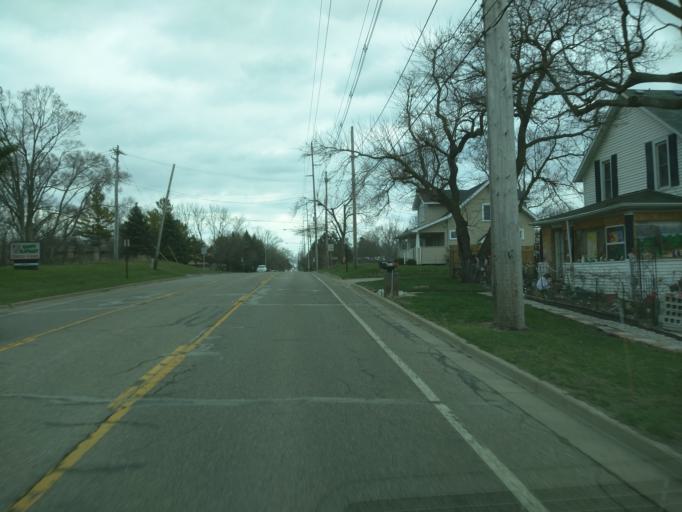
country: US
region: Michigan
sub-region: Ingham County
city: Lansing
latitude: 42.6980
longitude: -84.5234
